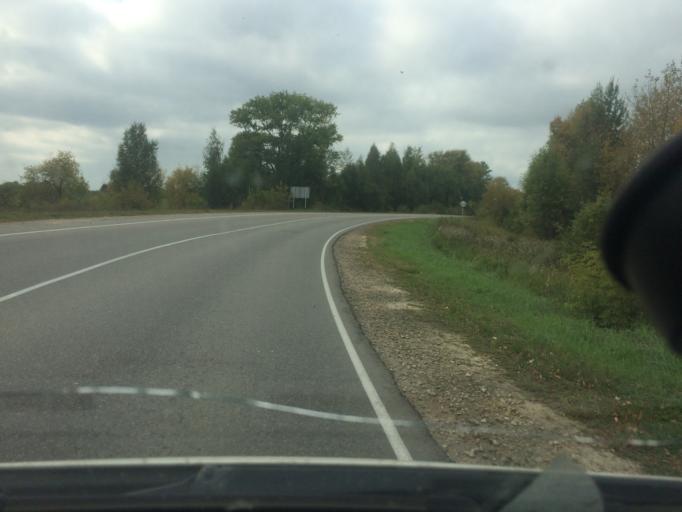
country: RU
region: Tula
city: Odoyev
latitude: 53.9888
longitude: 36.7148
